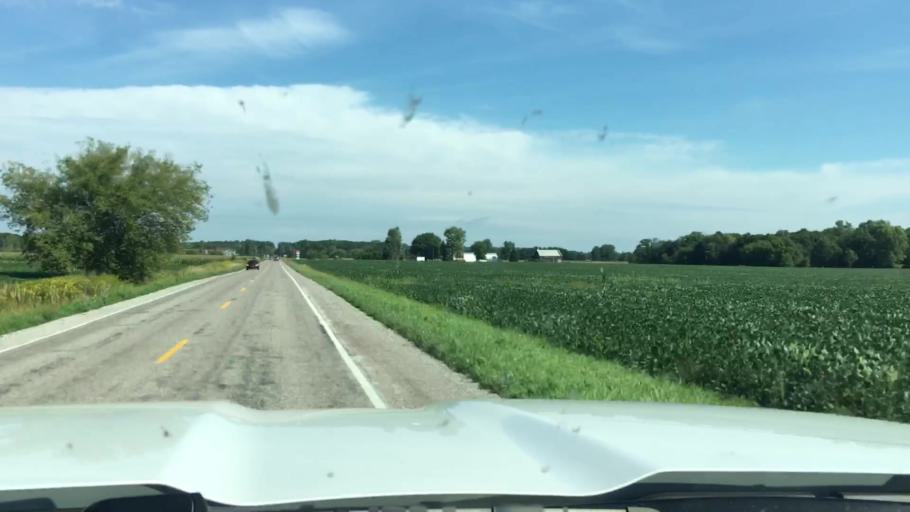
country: US
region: Michigan
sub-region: Saginaw County
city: Hemlock
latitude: 43.4455
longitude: -84.2301
